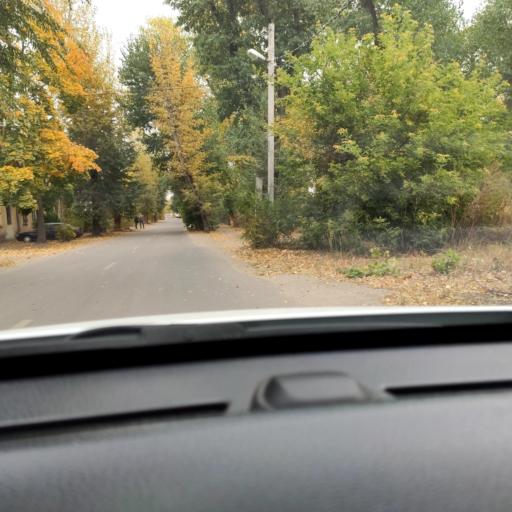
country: RU
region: Voronezj
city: Maslovka
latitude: 51.6153
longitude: 39.2530
